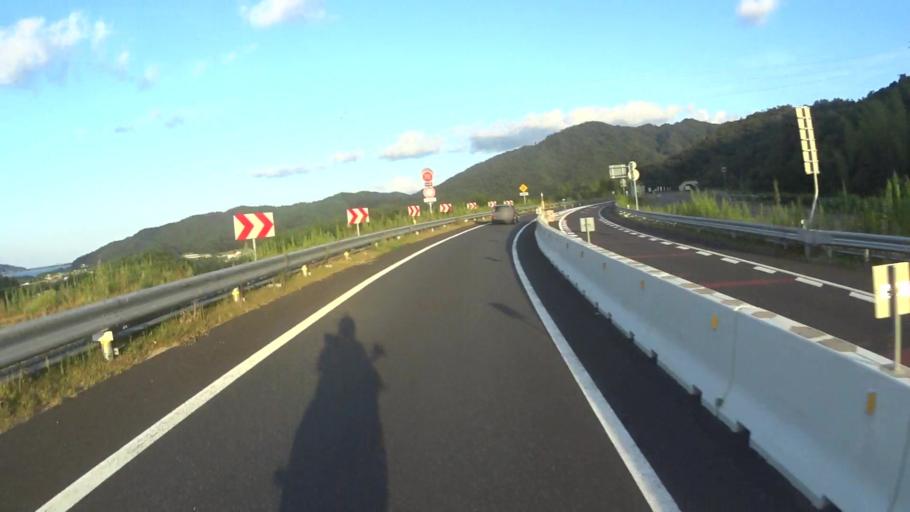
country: JP
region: Kyoto
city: Miyazu
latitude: 35.5492
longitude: 135.1457
